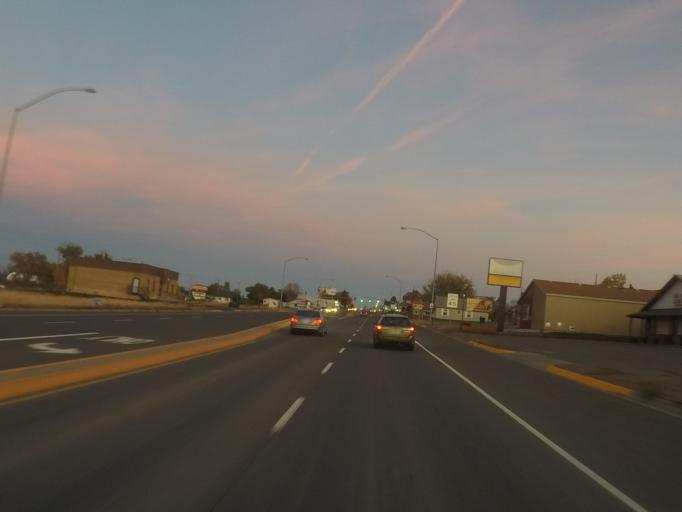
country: US
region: Montana
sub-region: Lewis and Clark County
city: Helena
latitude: 46.6072
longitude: -112.0699
